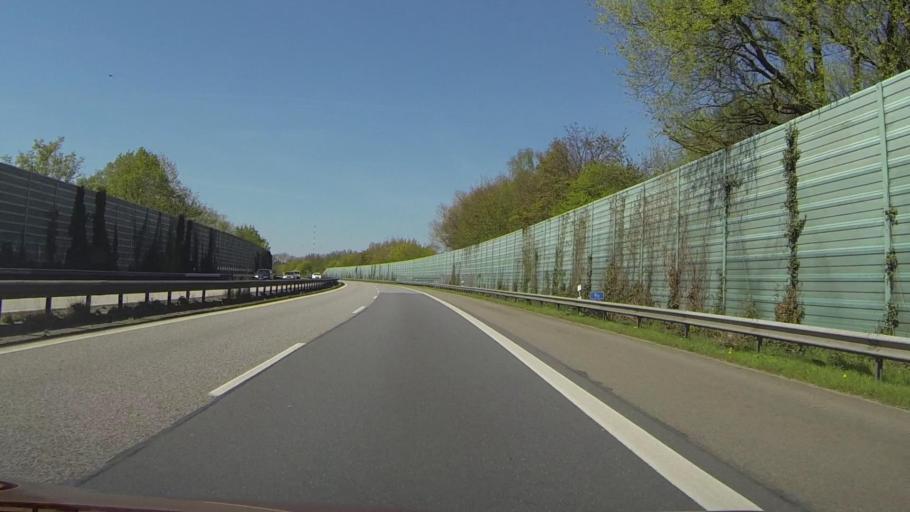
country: DE
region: Schleswig-Holstein
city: Rellingen
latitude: 53.6607
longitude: 9.8196
